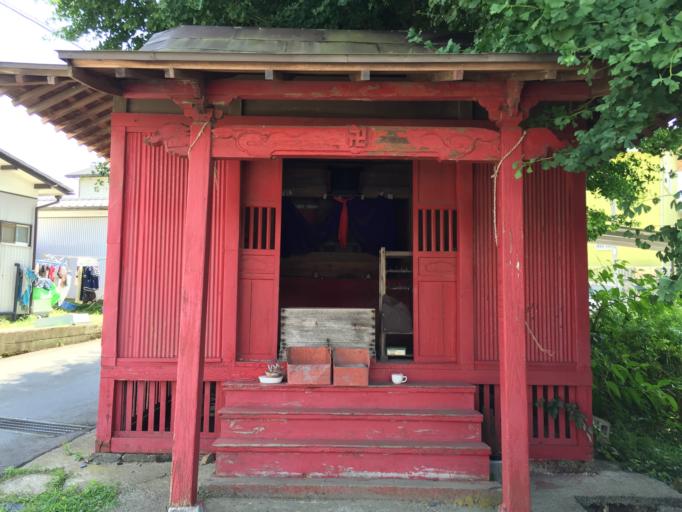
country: JP
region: Ibaraki
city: Oarai
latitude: 36.3193
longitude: 140.5691
